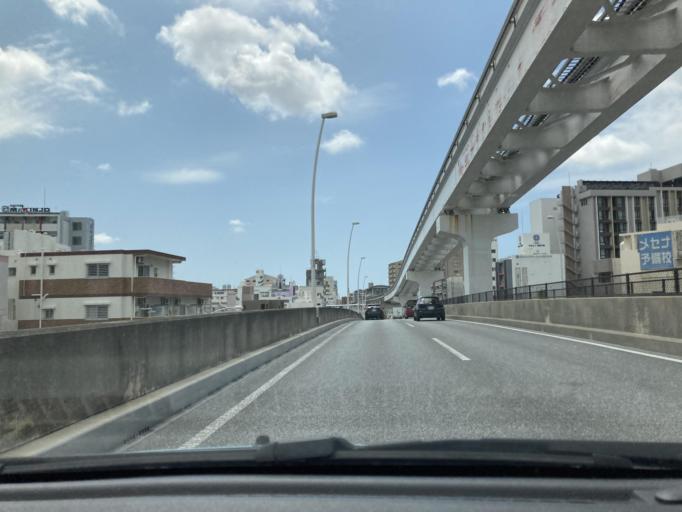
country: JP
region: Okinawa
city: Naha-shi
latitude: 26.2189
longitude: 127.6971
